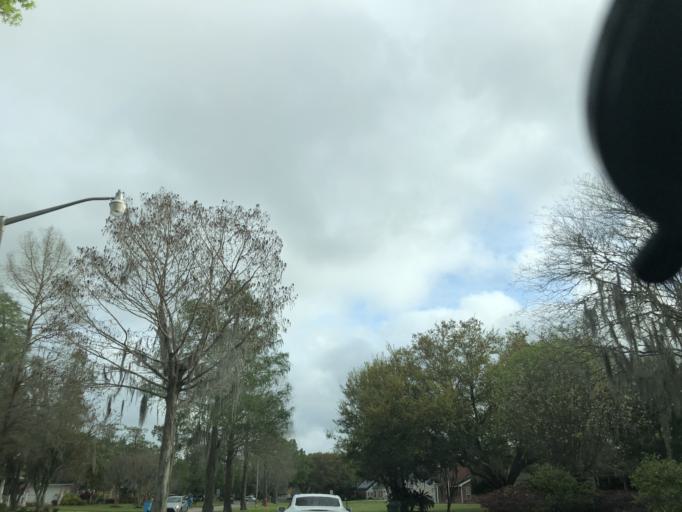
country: US
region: Louisiana
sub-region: Saint Charles Parish
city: New Sarpy
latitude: 29.9781
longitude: -90.3636
